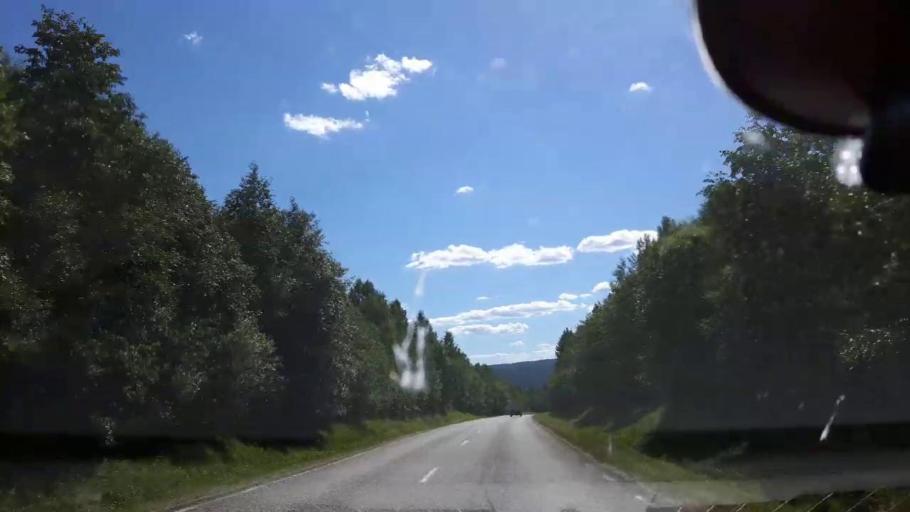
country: SE
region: Vaesternorrland
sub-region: Ange Kommun
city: Fransta
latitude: 62.8062
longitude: 16.2101
